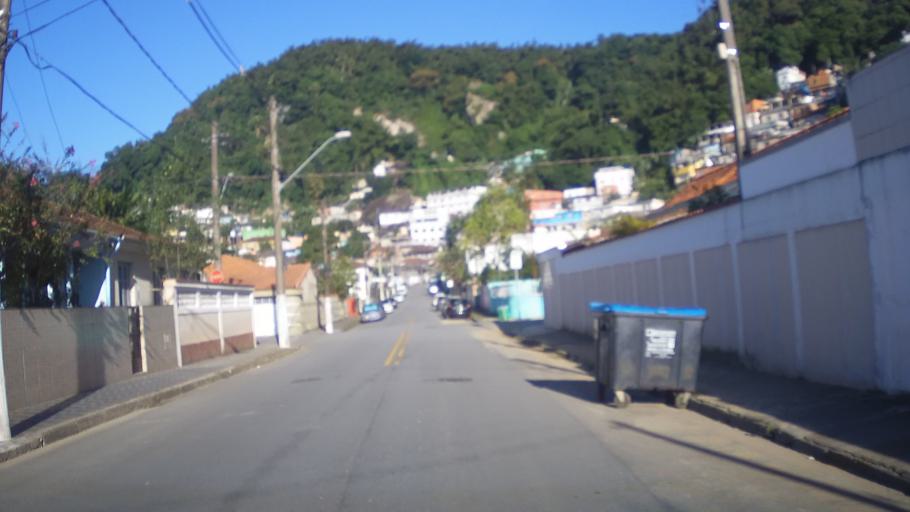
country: BR
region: Sao Paulo
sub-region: Santos
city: Santos
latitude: -23.9409
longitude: -46.3401
